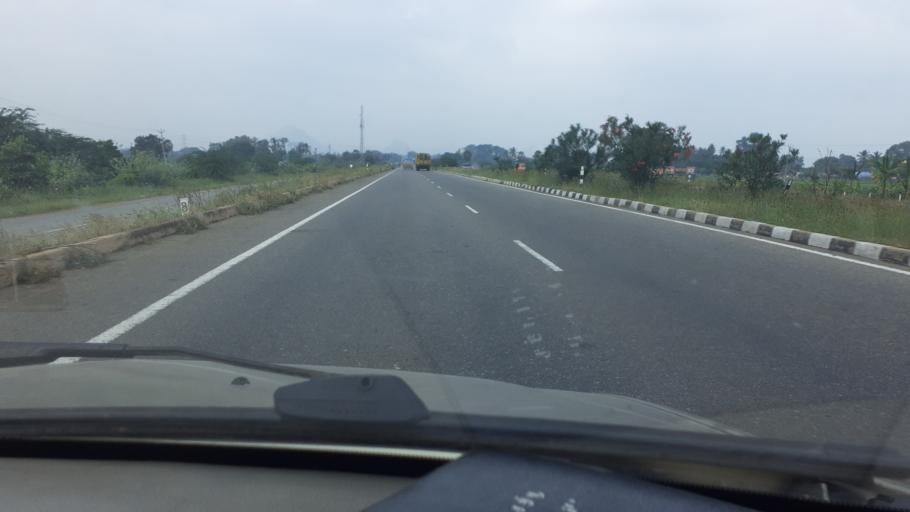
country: IN
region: Tamil Nadu
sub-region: Tirunelveli Kattabo
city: Nanguneri
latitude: 8.4869
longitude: 77.6563
